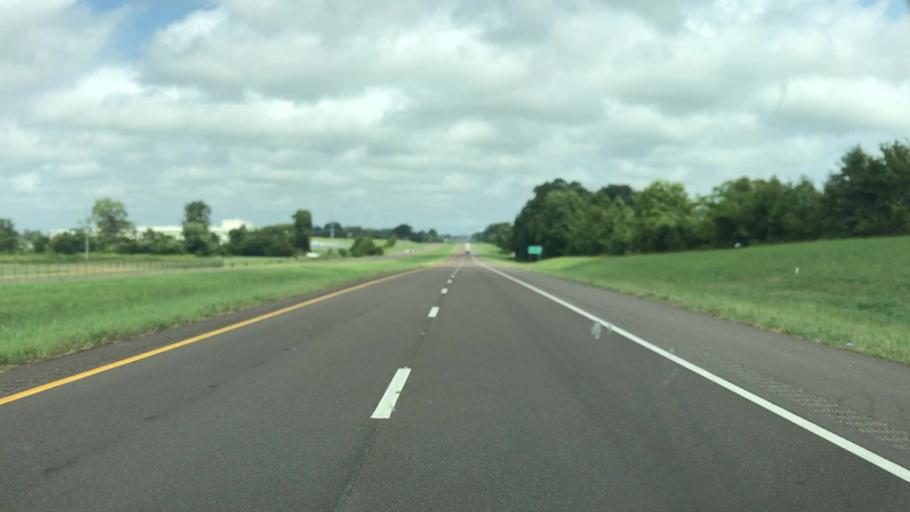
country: US
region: Tennessee
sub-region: Dyer County
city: Dyersburg
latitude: 36.0775
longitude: -89.3409
